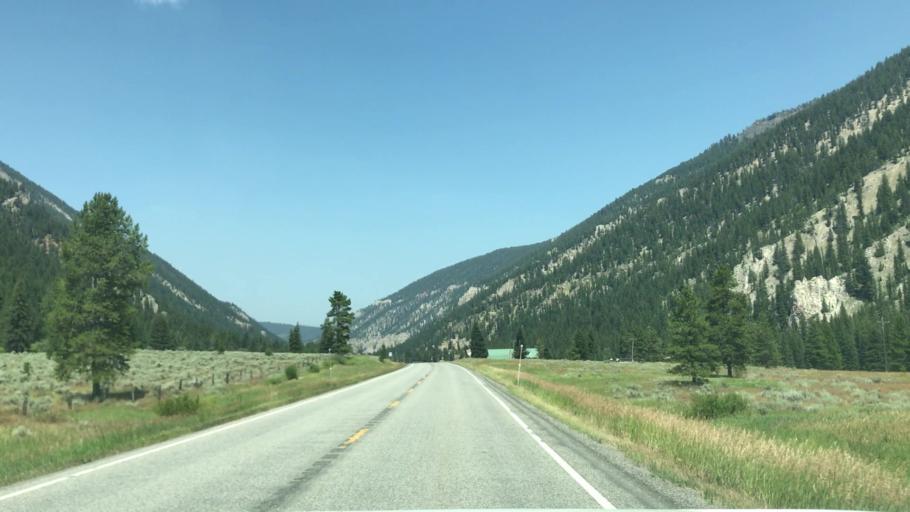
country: US
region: Montana
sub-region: Gallatin County
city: Big Sky
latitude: 45.1125
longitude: -111.2243
